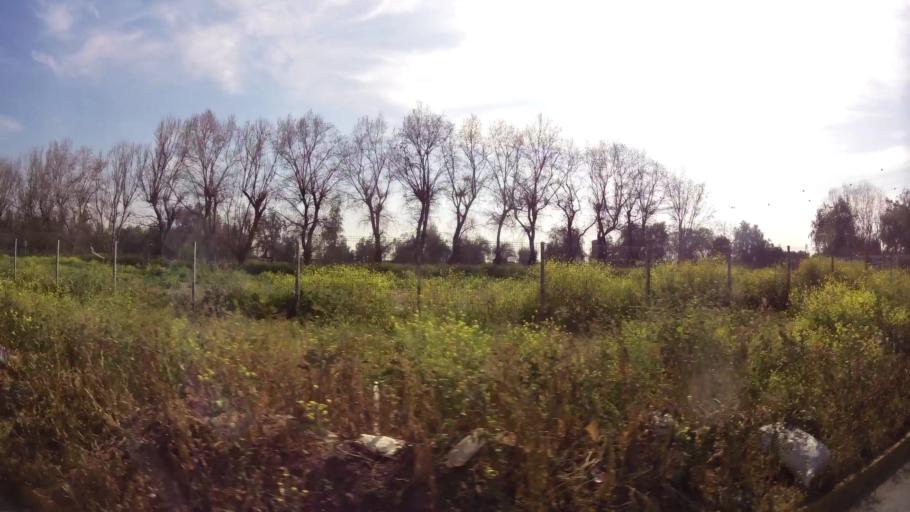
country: CL
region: Santiago Metropolitan
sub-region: Provincia de Santiago
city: Lo Prado
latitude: -33.4554
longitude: -70.7325
